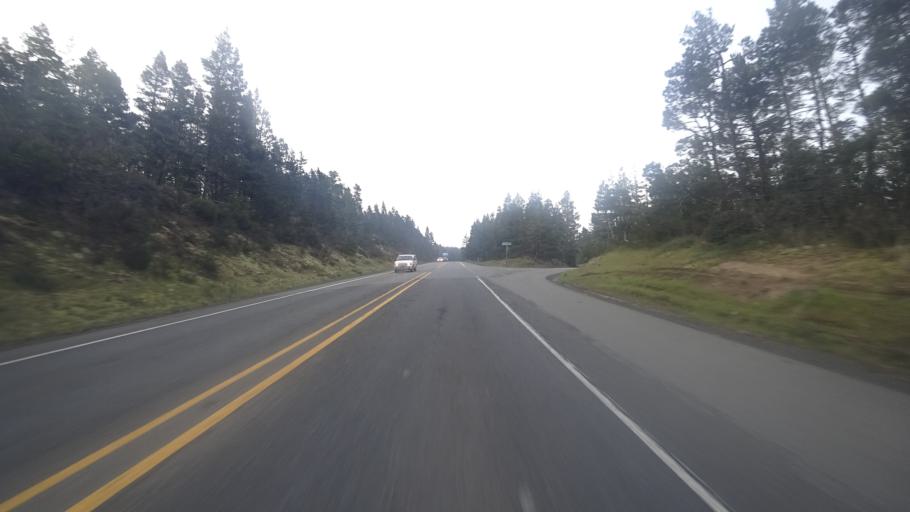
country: US
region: Oregon
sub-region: Coos County
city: Lakeside
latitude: 43.6320
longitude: -124.1844
